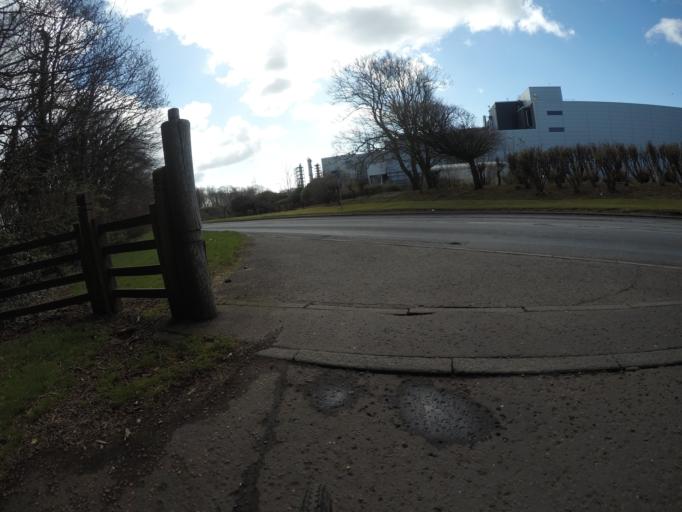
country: GB
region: Scotland
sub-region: North Ayrshire
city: Dreghorn
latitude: 55.5963
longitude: -4.6258
